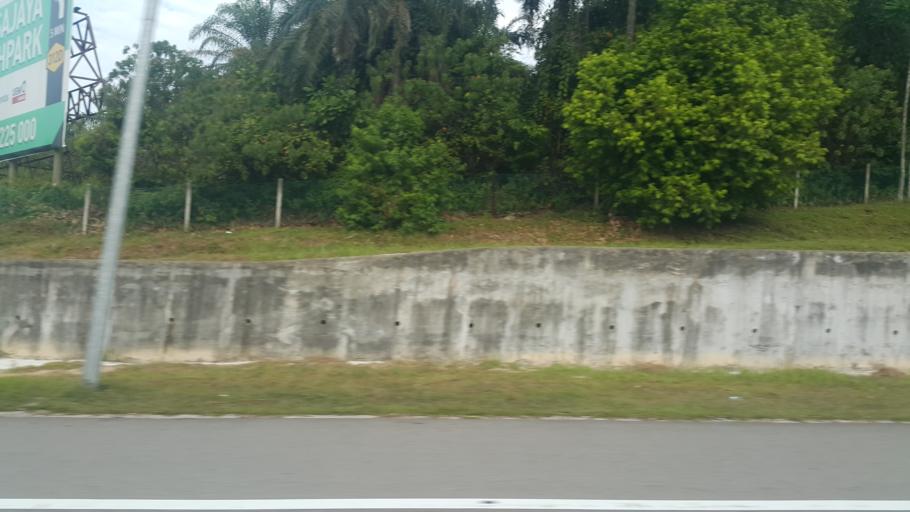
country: MY
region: Johor
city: Pekan Nenas
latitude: 1.4248
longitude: 103.6021
